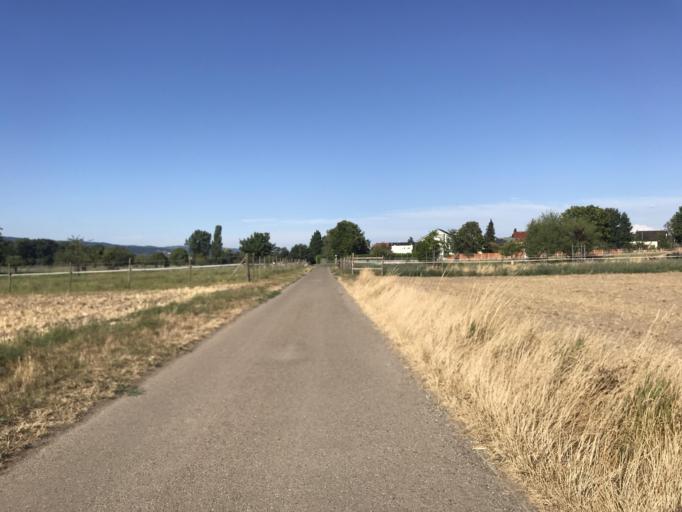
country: DE
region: Rheinland-Pfalz
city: Gau-Algesheim
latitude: 49.9753
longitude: 8.0045
